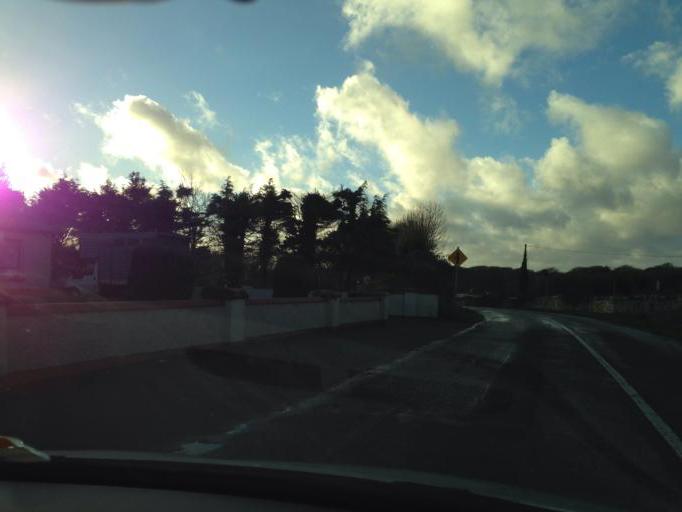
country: IE
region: Connaught
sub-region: County Galway
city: Oranmore
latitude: 53.2725
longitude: -8.9804
